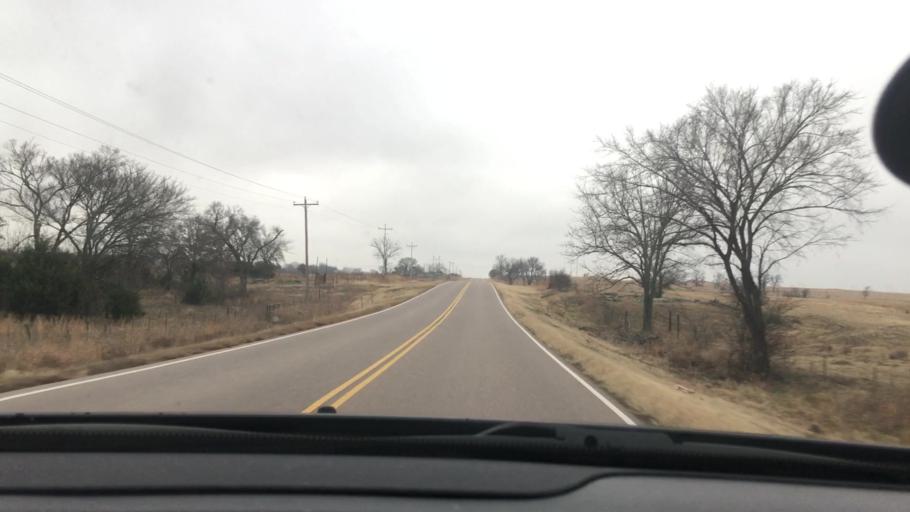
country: US
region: Oklahoma
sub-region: Johnston County
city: Tishomingo
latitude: 34.3746
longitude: -96.6360
